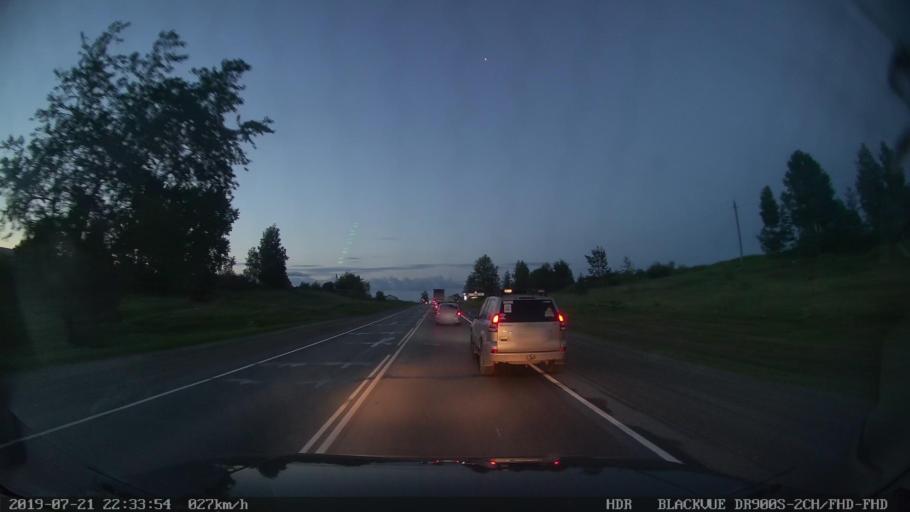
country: RU
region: Perm
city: Chaykovskaya
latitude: 58.0392
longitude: 55.5709
